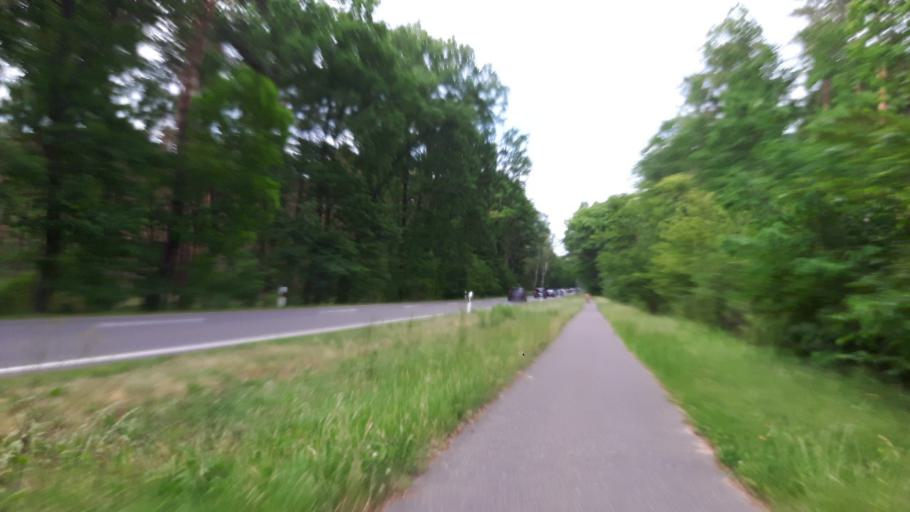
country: DE
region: Brandenburg
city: Michendorf
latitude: 52.3339
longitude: 13.0405
